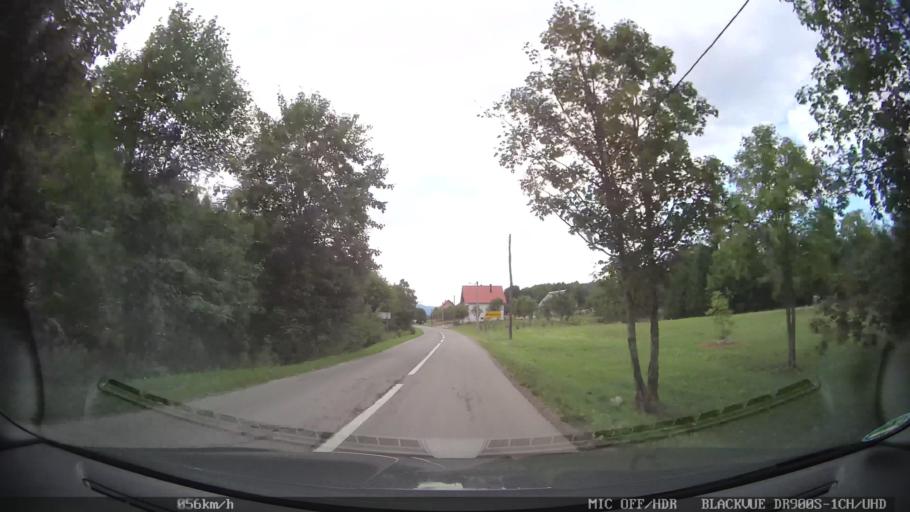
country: HR
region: Licko-Senjska
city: Jezerce
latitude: 44.9630
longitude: 15.5261
